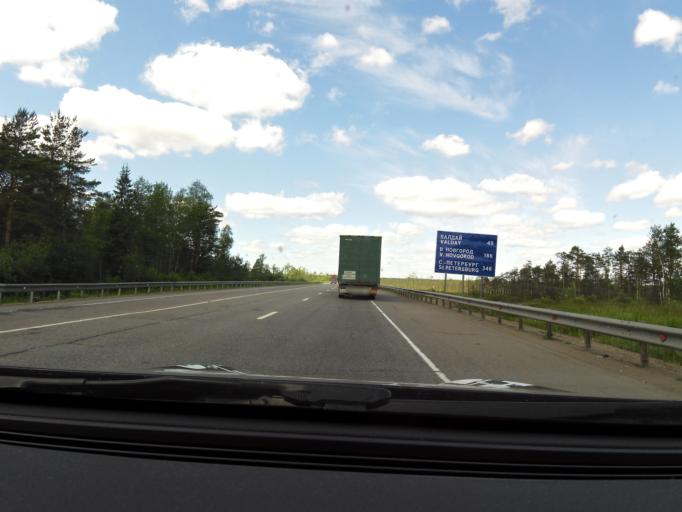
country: RU
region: Tverskaya
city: Kuzhenkino
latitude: 57.7686
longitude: 33.9367
